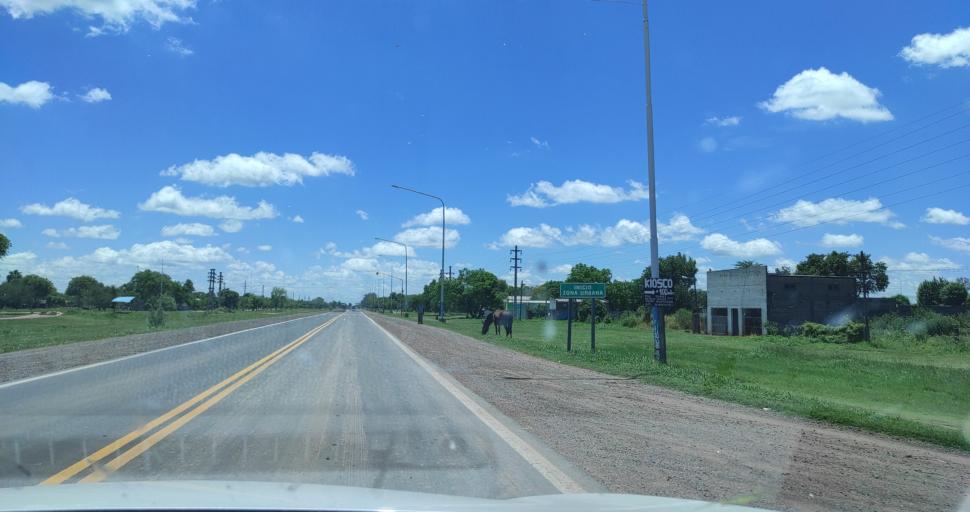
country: AR
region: Chaco
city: Campo Largo
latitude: -26.8108
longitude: -60.8412
